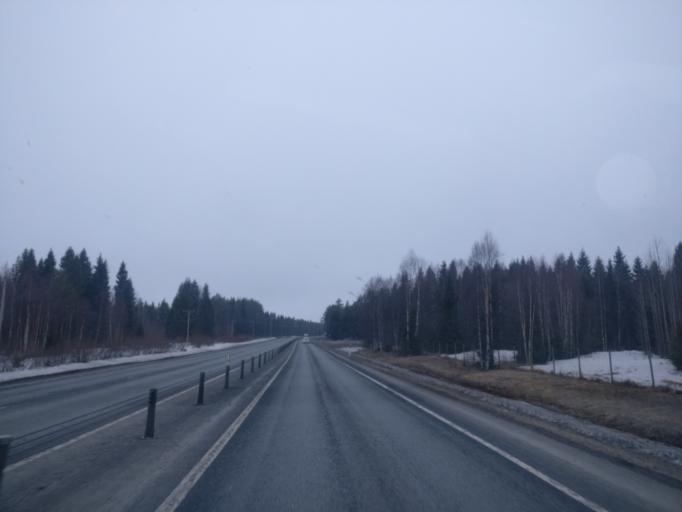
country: FI
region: Lapland
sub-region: Kemi-Tornio
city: Simo
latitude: 65.6688
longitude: 24.9496
